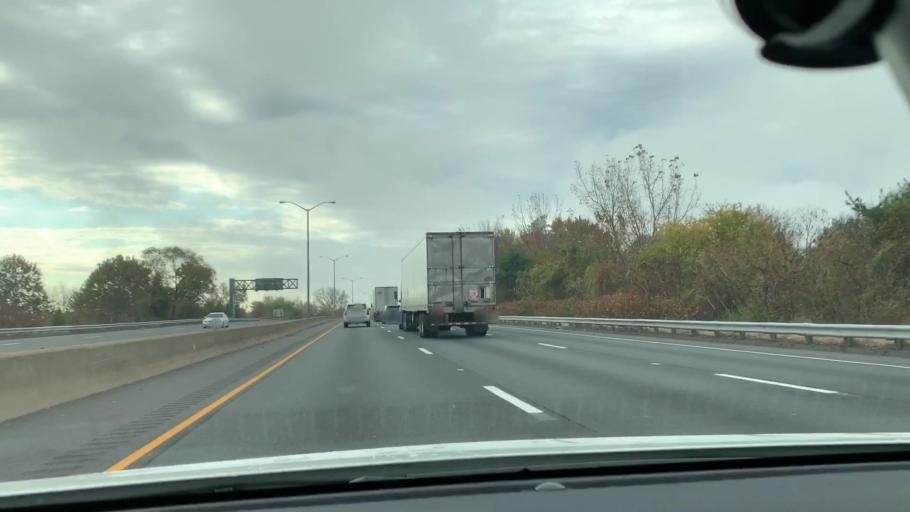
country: US
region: Connecticut
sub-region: Hartford County
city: Enfield
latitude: 41.9779
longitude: -72.5876
